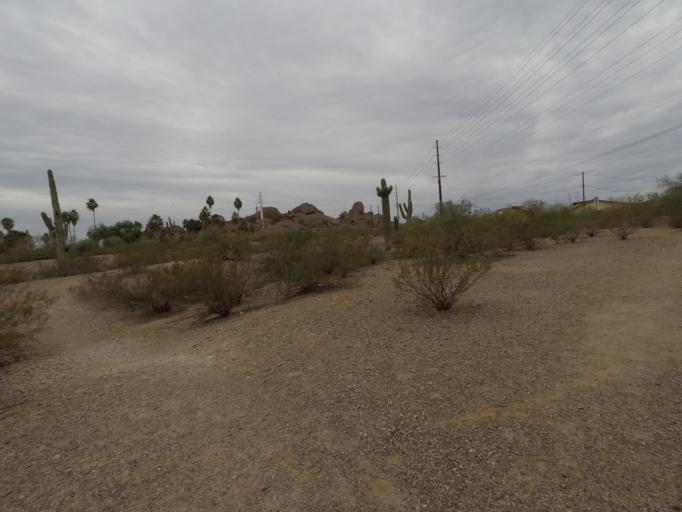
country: US
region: Arizona
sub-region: Maricopa County
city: Tempe Junction
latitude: 33.4508
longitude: -111.9367
